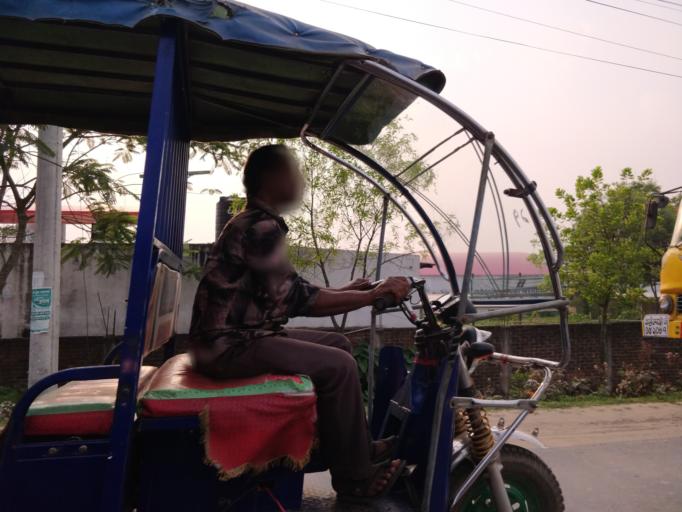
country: IN
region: Tripura
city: Khowai
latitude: 24.1342
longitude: 91.3519
